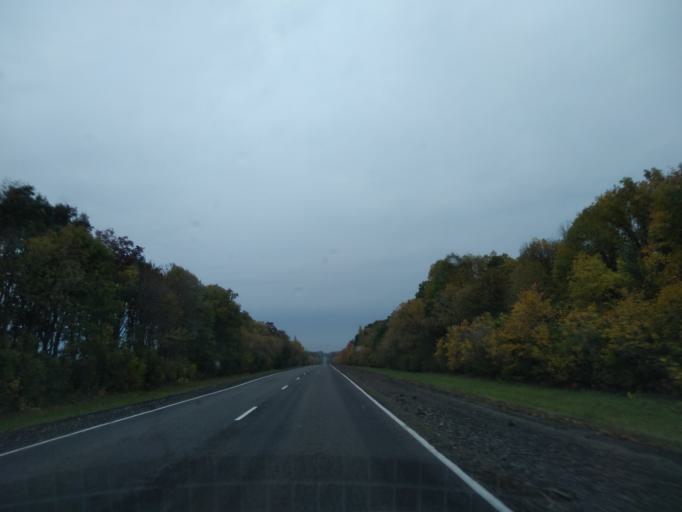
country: RU
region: Lipetsk
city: Zadonsk
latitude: 52.4705
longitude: 38.7693
